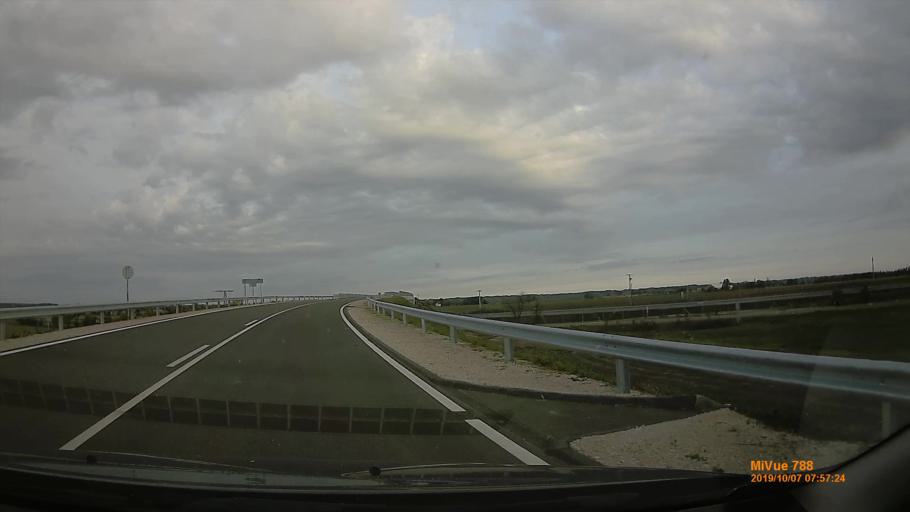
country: HU
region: Jasz-Nagykun-Szolnok
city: Cserkeszolo
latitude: 46.8782
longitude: 20.1434
